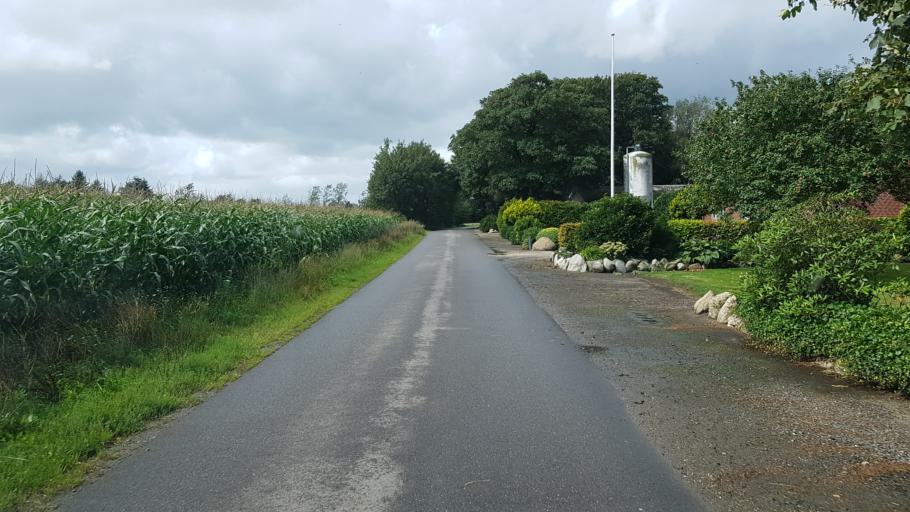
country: DK
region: South Denmark
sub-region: Vejen Kommune
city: Holsted
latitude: 55.5966
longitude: 8.8659
